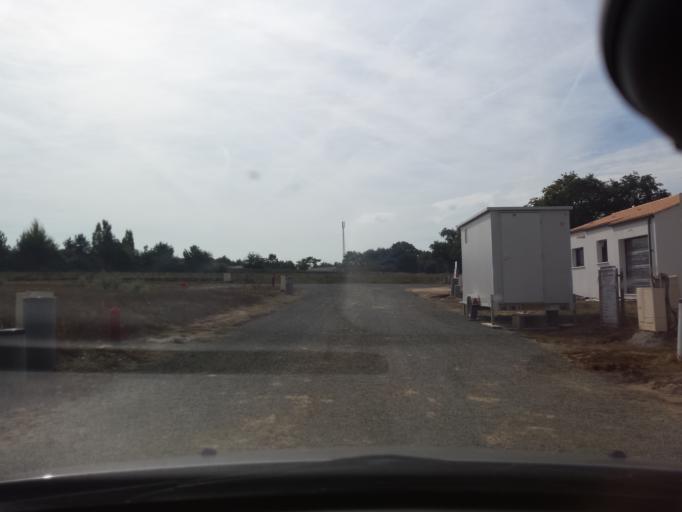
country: FR
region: Pays de la Loire
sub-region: Departement de la Vendee
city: Nieul-le-Dolent
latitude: 46.5724
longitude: -1.5147
